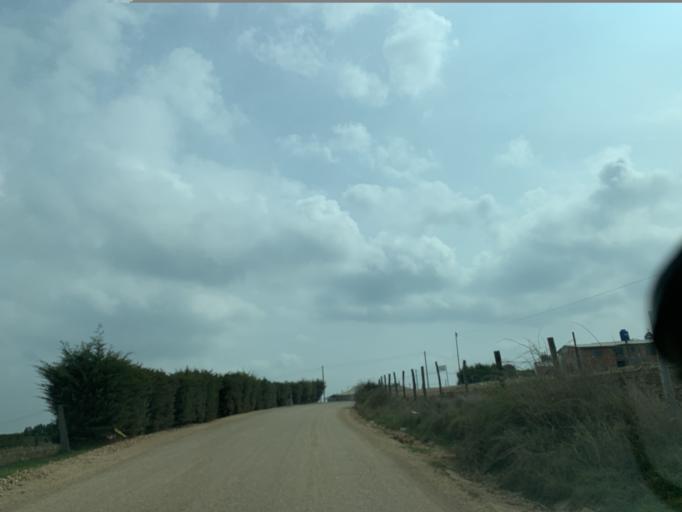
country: CO
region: Boyaca
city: Siachoque
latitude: 5.5468
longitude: -73.2994
